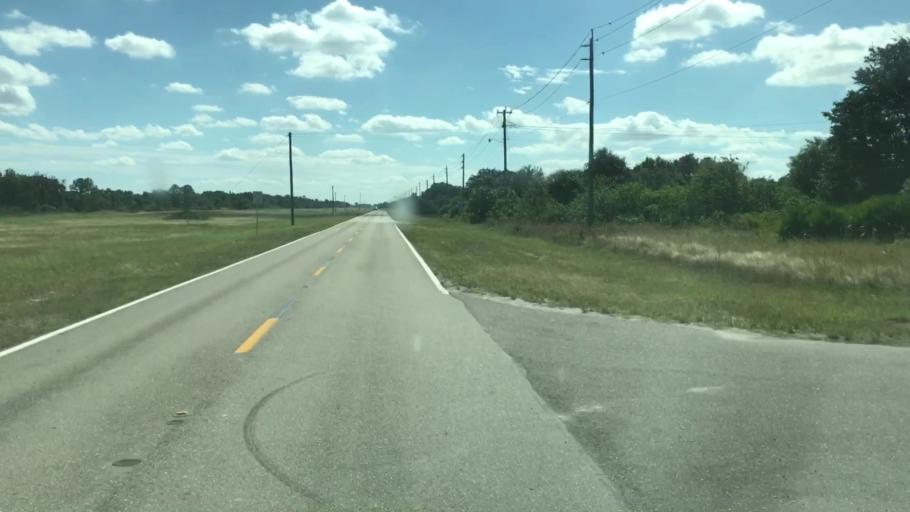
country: US
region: Florida
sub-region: Lee County
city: Olga
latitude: 26.6802
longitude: -81.6638
